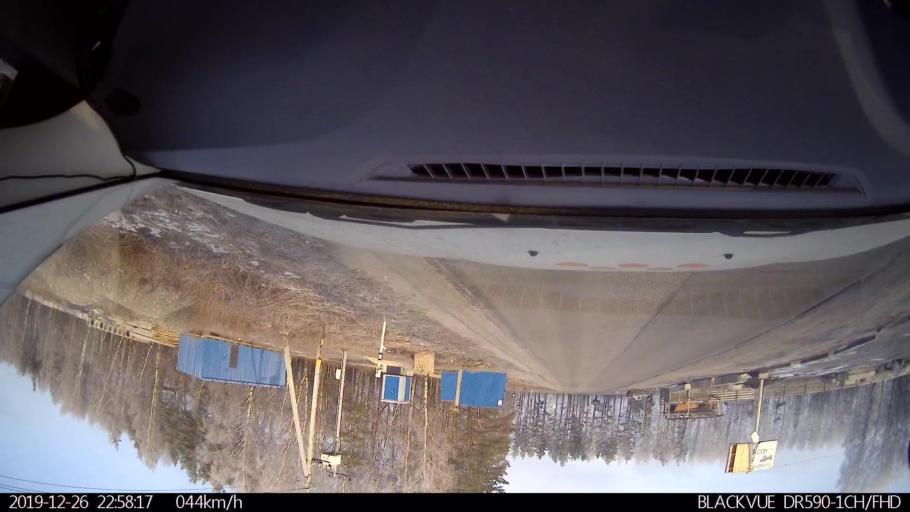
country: RU
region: Nizjnij Novgorod
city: Burevestnik
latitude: 56.1566
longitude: 43.7091
